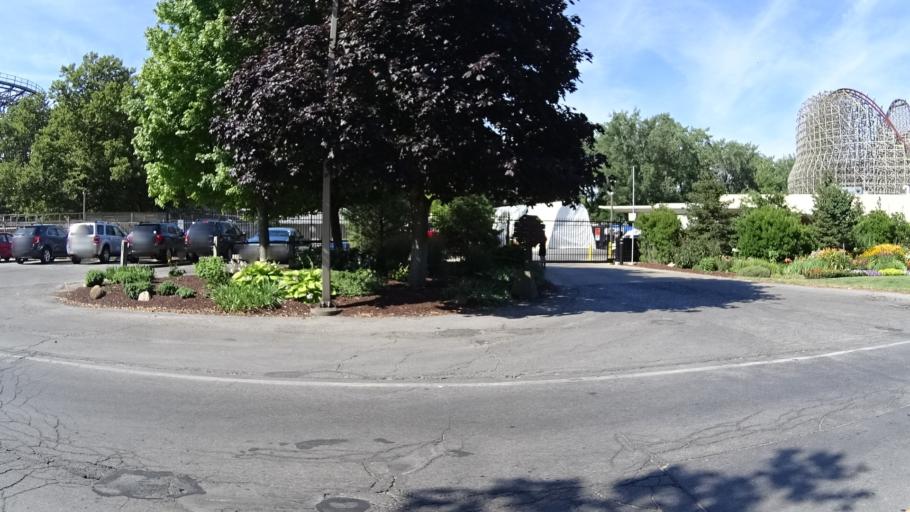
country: US
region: Ohio
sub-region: Erie County
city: Sandusky
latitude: 41.4872
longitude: -82.6896
